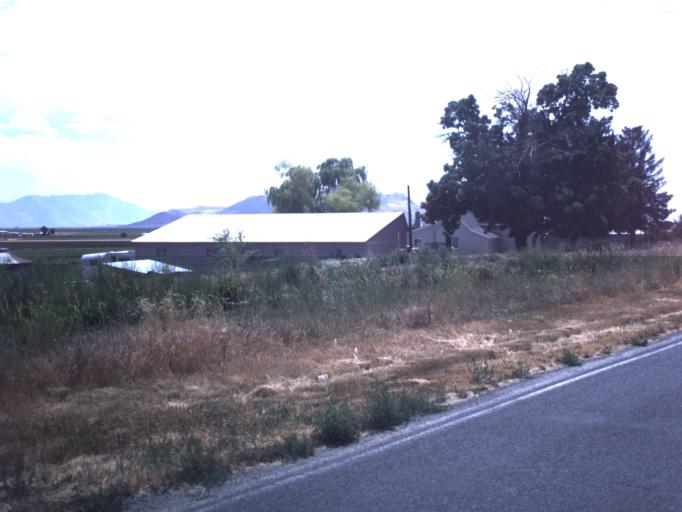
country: US
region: Utah
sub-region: Box Elder County
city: Tremonton
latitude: 41.6919
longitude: -112.2955
